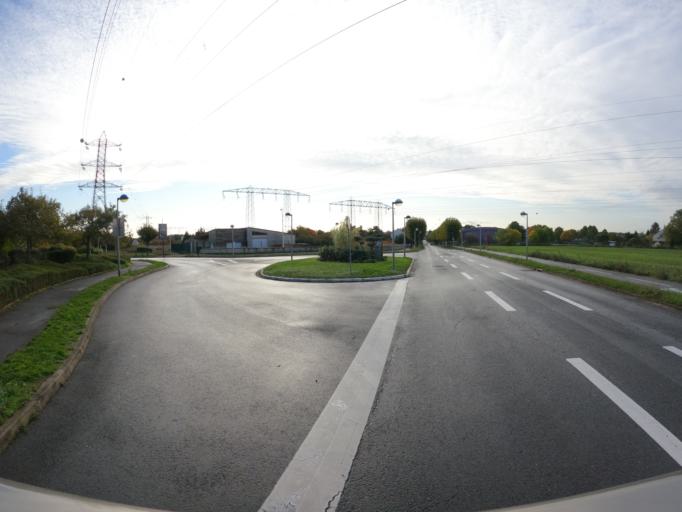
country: FR
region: Ile-de-France
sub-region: Departement de Seine-et-Marne
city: Brou-sur-Chantereine
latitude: 48.8897
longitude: 2.6197
